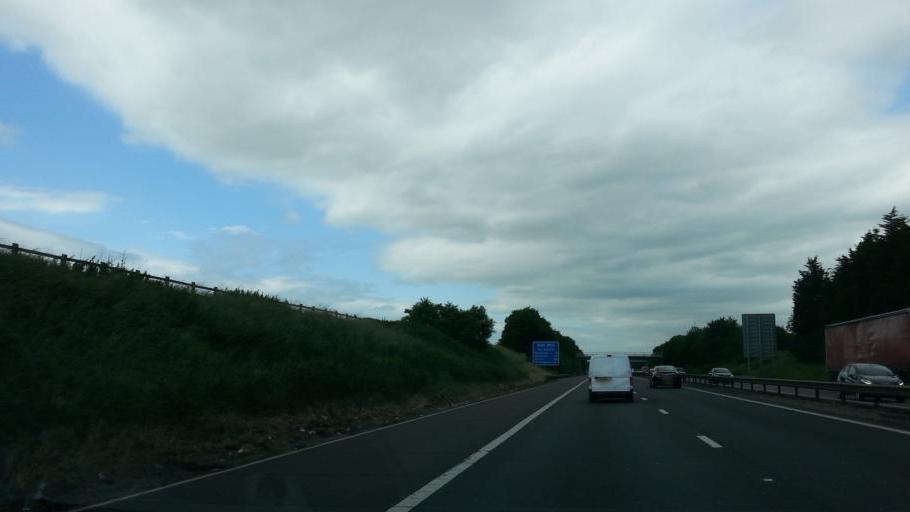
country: GB
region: England
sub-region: Warwickshire
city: Curdworth
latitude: 52.5519
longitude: -1.7140
